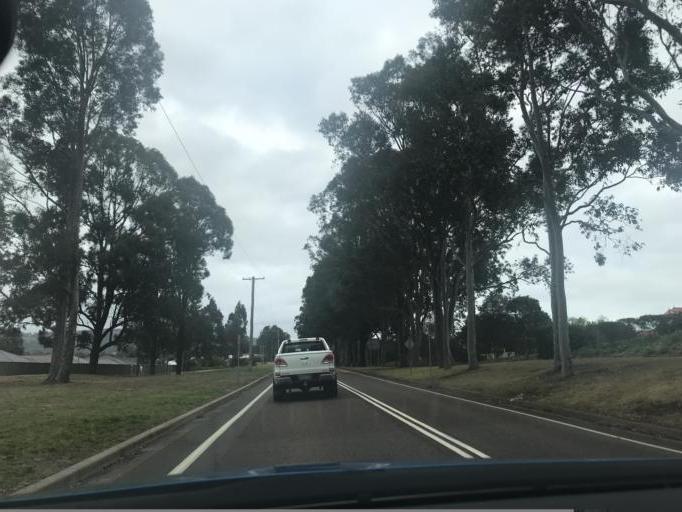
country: AU
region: New South Wales
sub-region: Cessnock
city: Cessnock
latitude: -32.8293
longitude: 151.3303
